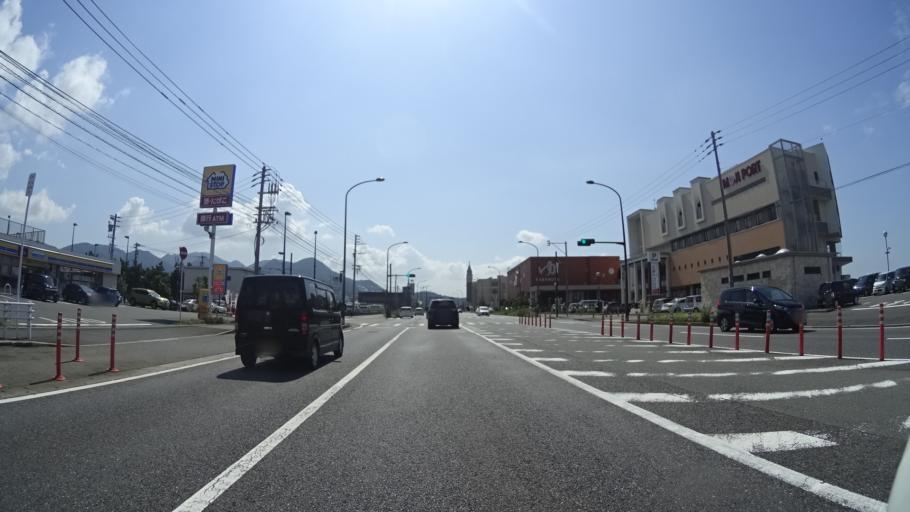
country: JP
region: Yamaguchi
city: Shimonoseki
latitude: 33.9033
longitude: 130.9277
